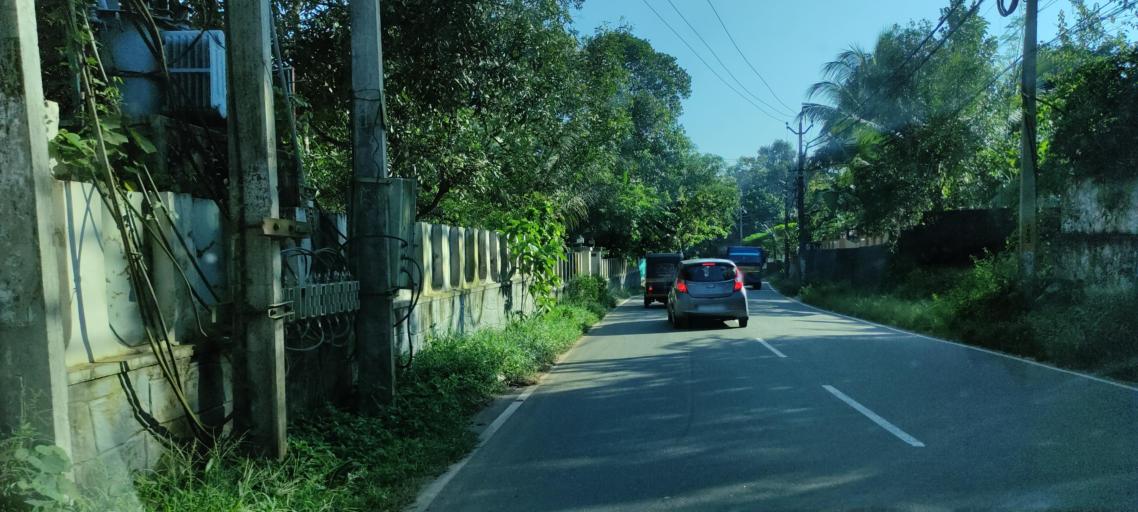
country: IN
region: Kerala
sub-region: Pattanamtitta
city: Adur
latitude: 9.1675
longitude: 76.7413
